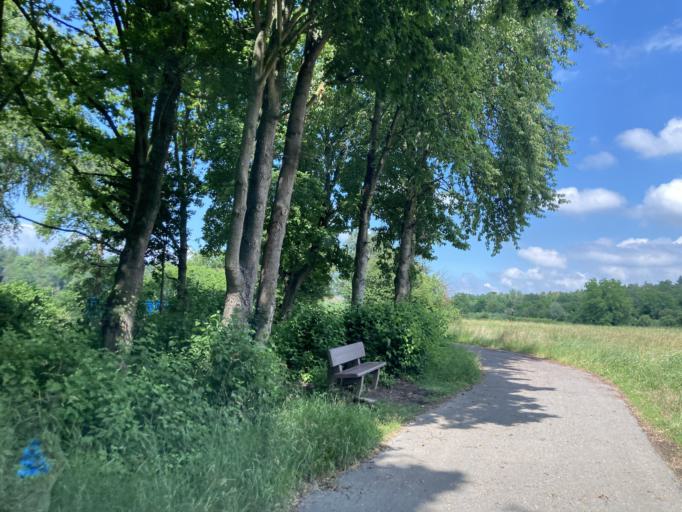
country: DE
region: Baden-Wuerttemberg
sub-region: Karlsruhe Region
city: Graben-Neudorf
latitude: 49.1873
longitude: 8.5083
